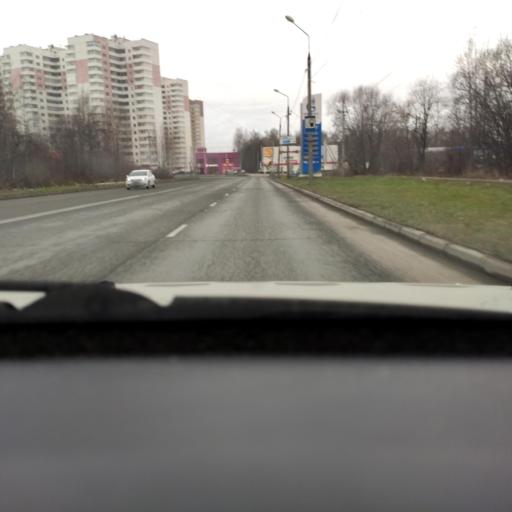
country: RU
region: Perm
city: Polazna
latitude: 58.1319
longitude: 56.4045
